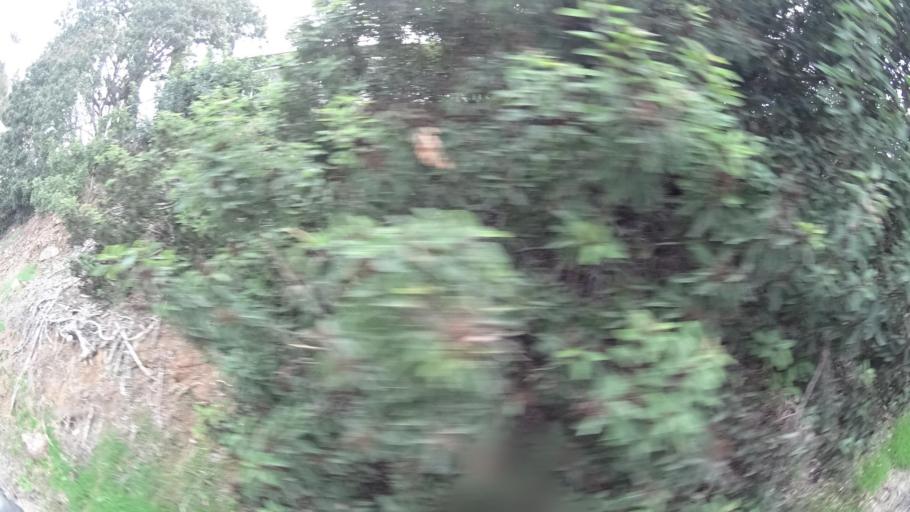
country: US
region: California
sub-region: San Diego County
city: Spring Valley
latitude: 32.7471
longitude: -117.0096
